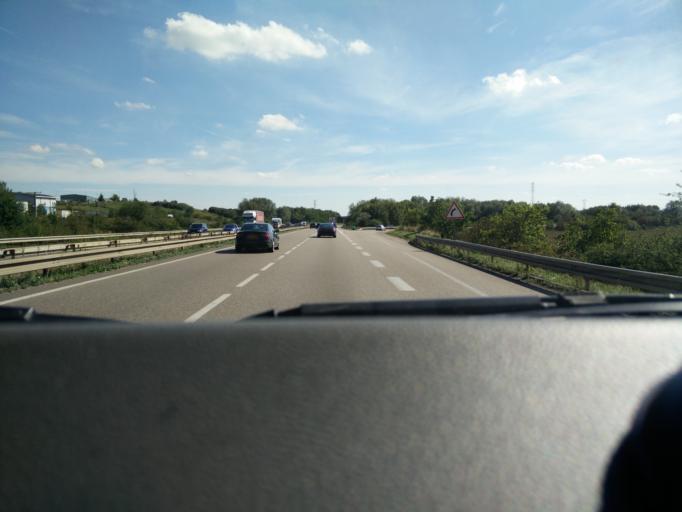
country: FR
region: Lorraine
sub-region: Departement de la Moselle
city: Bertrange
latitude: 49.3045
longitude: 6.1835
